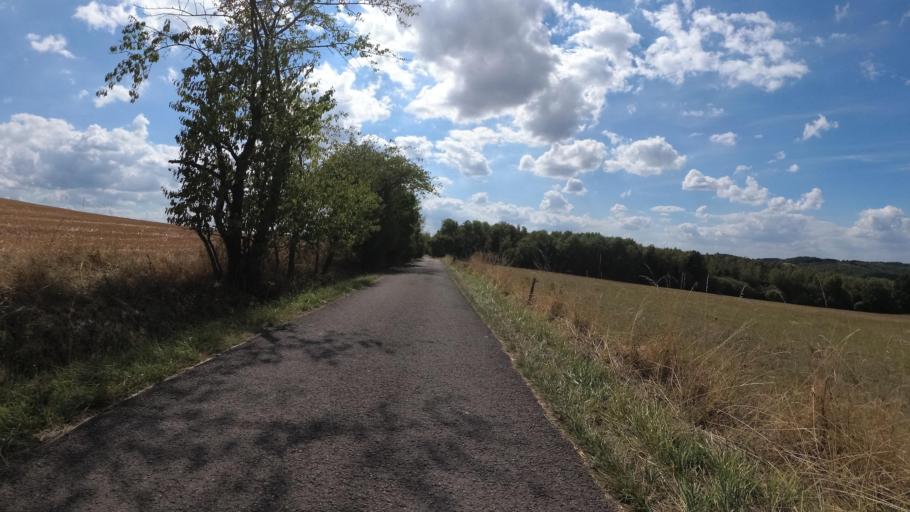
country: DE
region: Saarland
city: Mainzweiler
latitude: 49.4141
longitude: 7.0976
